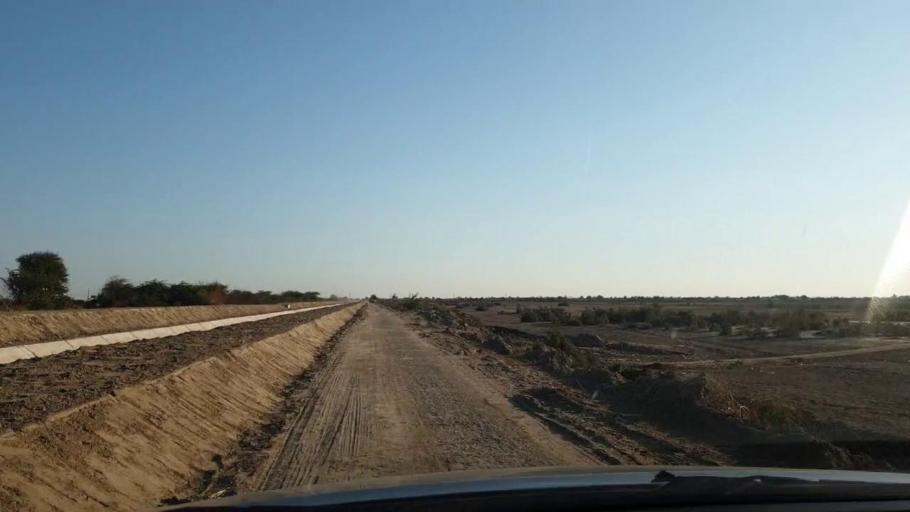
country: PK
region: Sindh
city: Tando Mittha Khan
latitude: 25.8459
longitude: 69.1717
